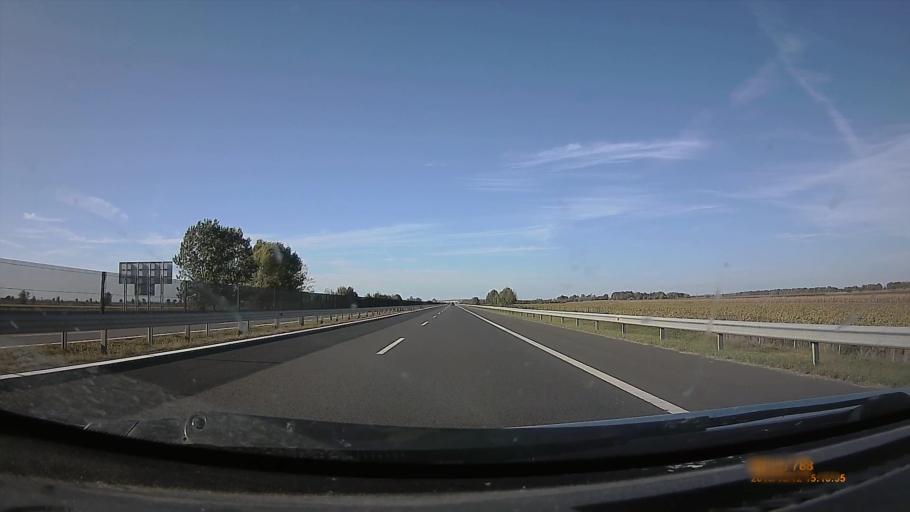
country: HU
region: Hajdu-Bihar
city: Hajduboszormeny
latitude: 47.6703
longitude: 21.4647
